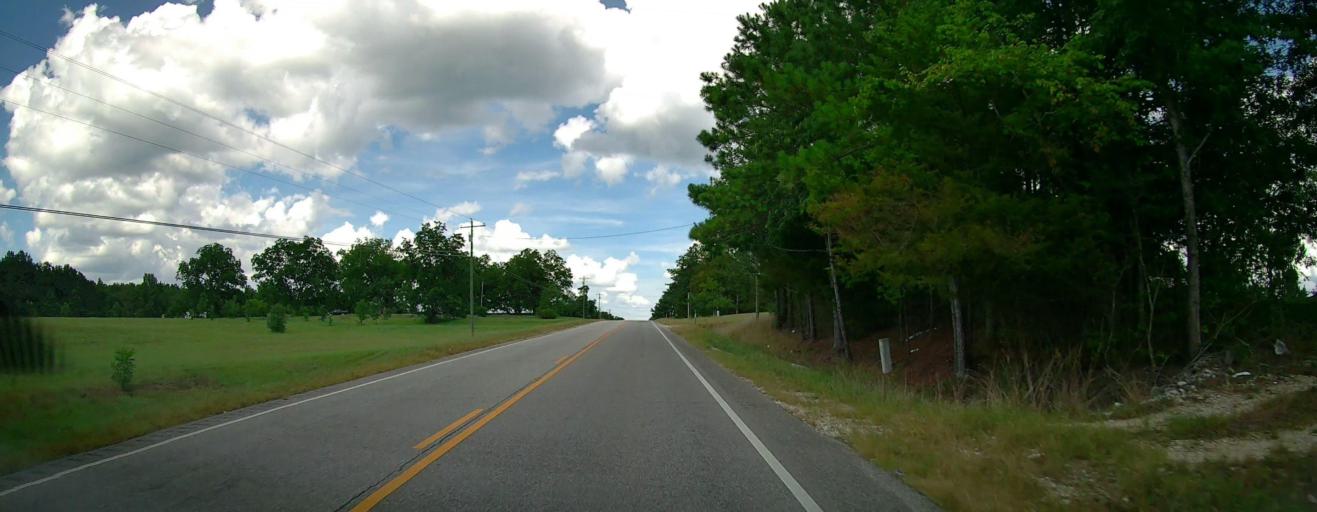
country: US
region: Alabama
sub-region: Macon County
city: Tuskegee
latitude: 32.4652
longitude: -85.5949
